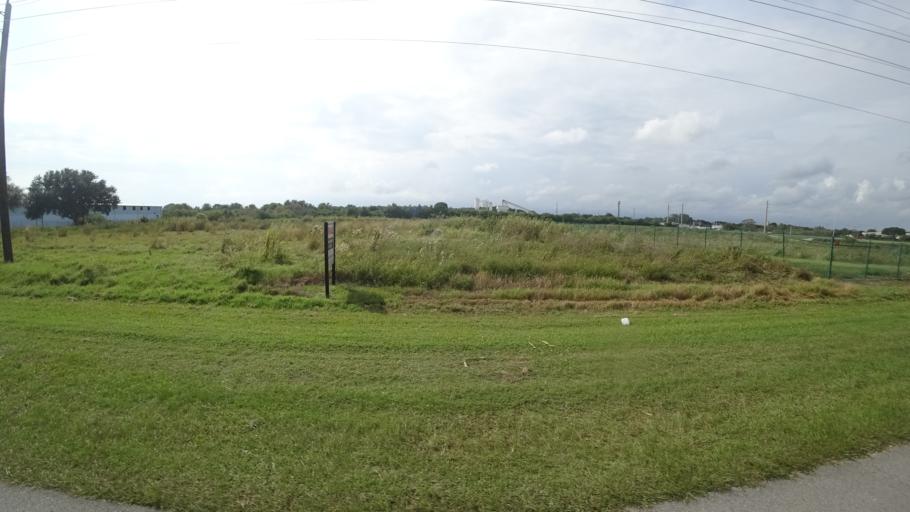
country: US
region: Florida
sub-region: Manatee County
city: Samoset
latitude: 27.4599
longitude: -82.5425
